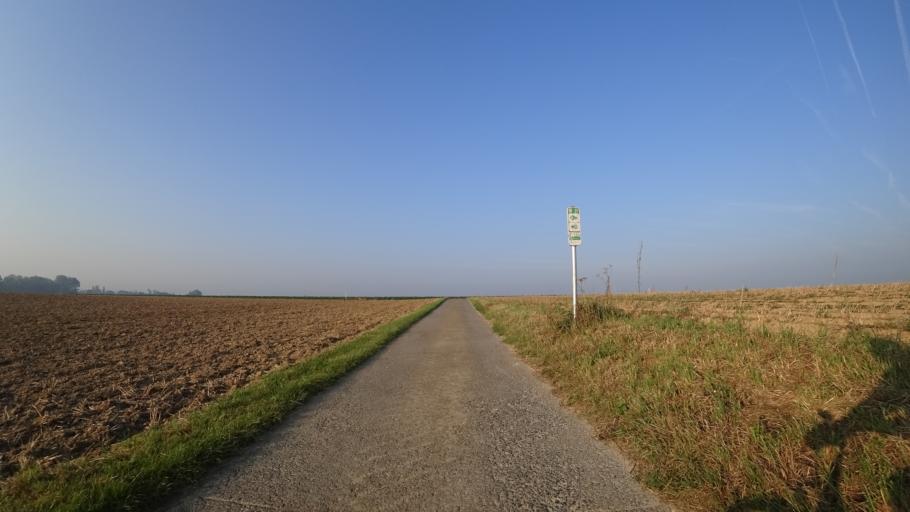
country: BE
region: Wallonia
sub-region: Province du Brabant Wallon
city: Walhain-Saint-Paul
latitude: 50.6036
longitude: 4.6795
